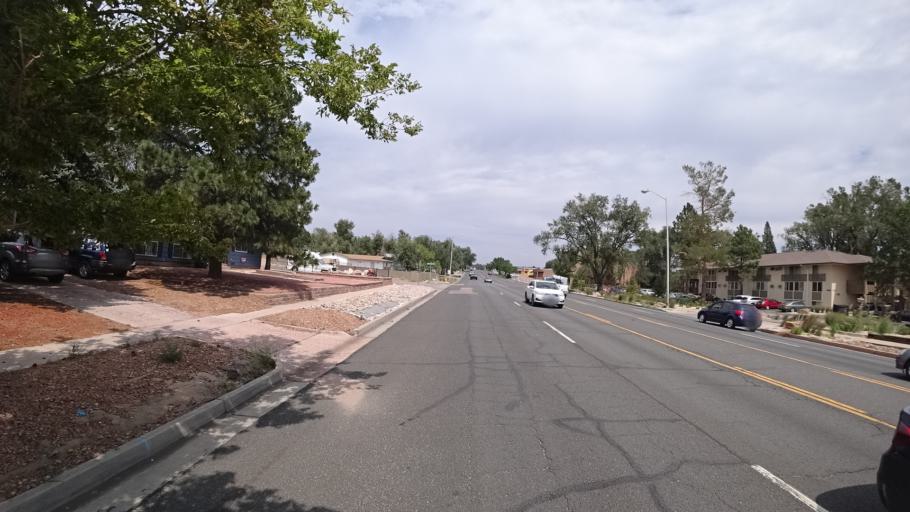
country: US
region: Colorado
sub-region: El Paso County
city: Colorado Springs
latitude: 38.8206
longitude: -104.7806
